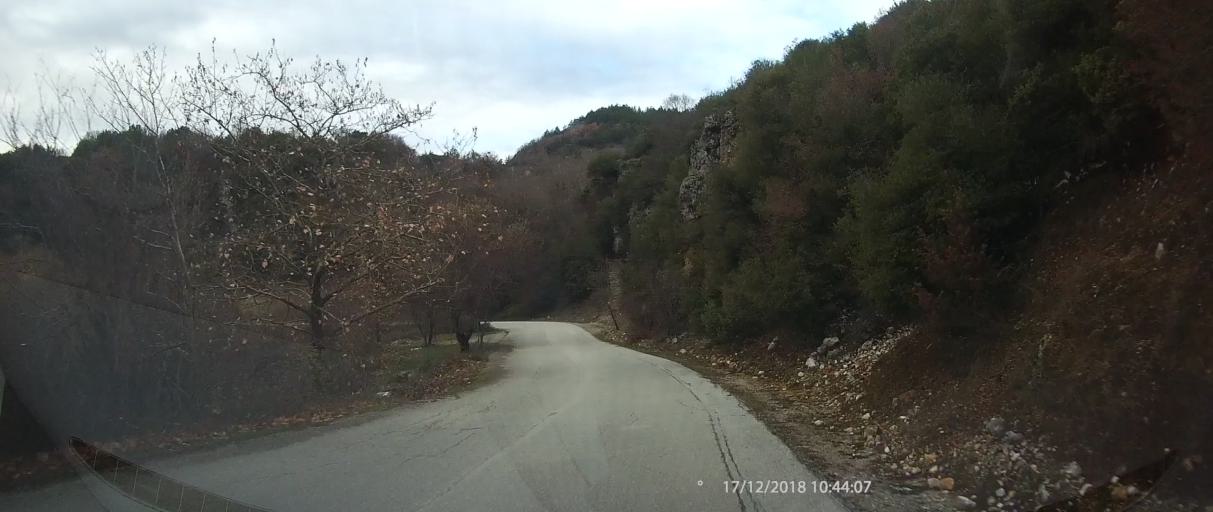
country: GR
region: Epirus
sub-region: Nomos Ioanninon
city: Konitsa
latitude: 39.9717
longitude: 20.7254
